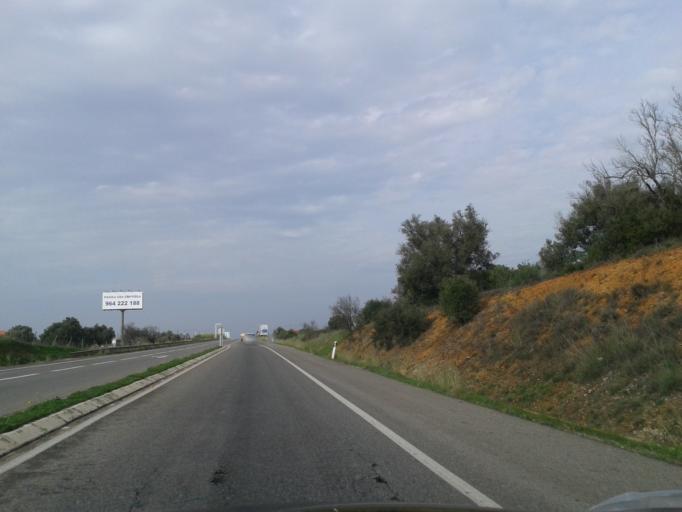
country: PT
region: Faro
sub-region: Albufeira
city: Ferreiras
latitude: 37.1211
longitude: -8.2495
